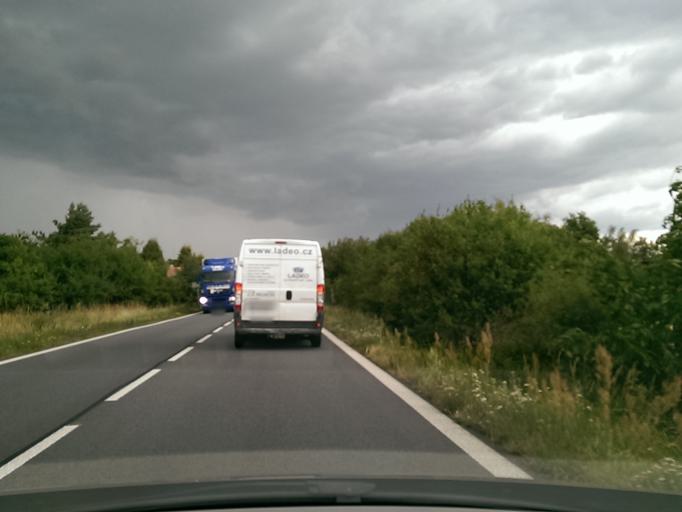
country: CZ
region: Central Bohemia
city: Loucen
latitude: 50.2550
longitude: 14.9877
